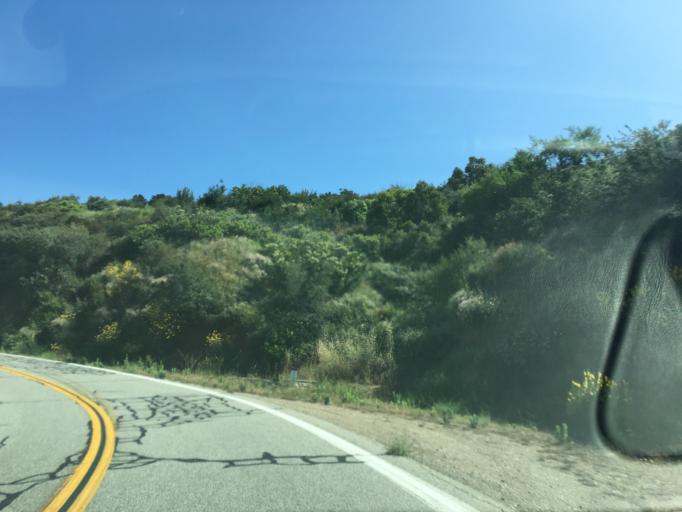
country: US
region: California
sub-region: Los Angeles County
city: Glendora
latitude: 34.1983
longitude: -117.8351
